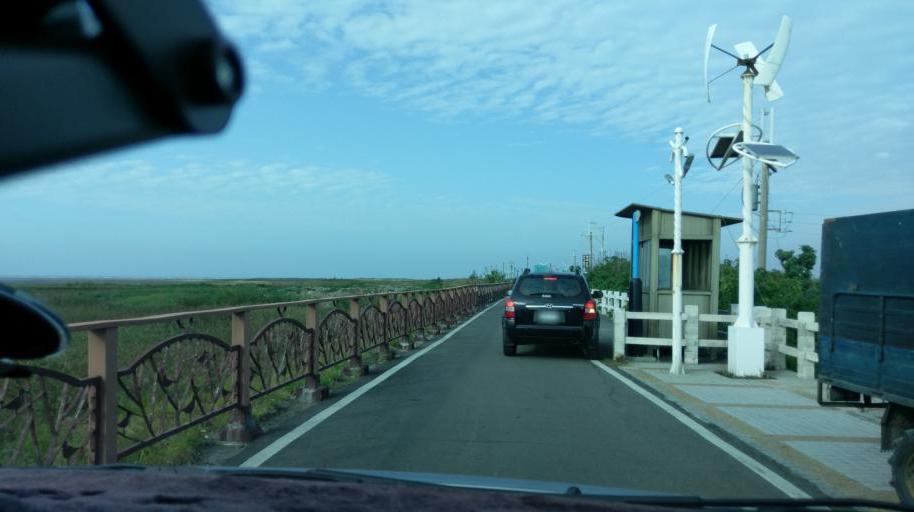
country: TW
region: Taiwan
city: Fengyuan
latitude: 24.3206
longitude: 120.5524
